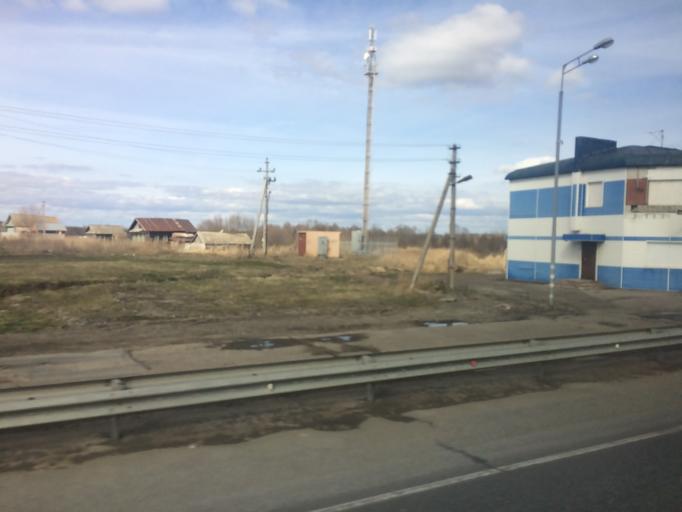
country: RU
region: Tatarstan
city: Nizhniye Vyazovyye
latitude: 55.7216
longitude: 48.5553
